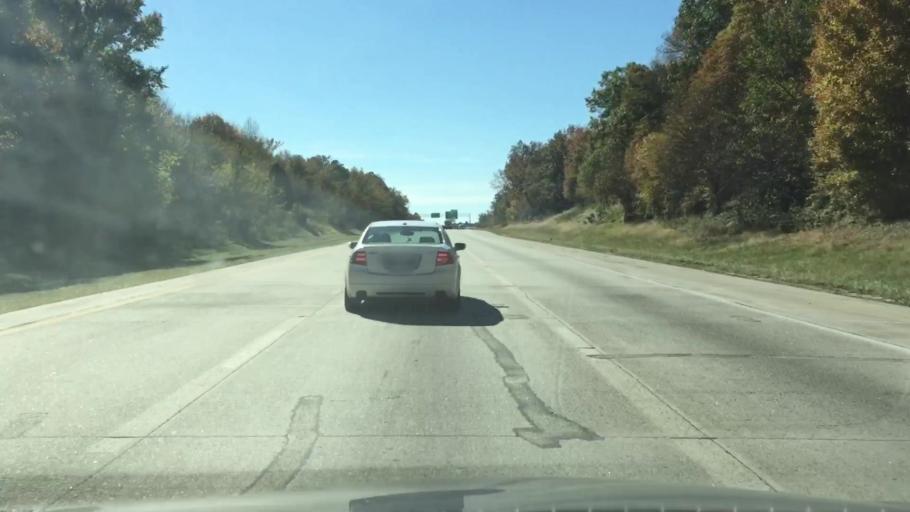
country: US
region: North Carolina
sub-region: Guilford County
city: Jamestown
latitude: 35.9370
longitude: -79.9117
